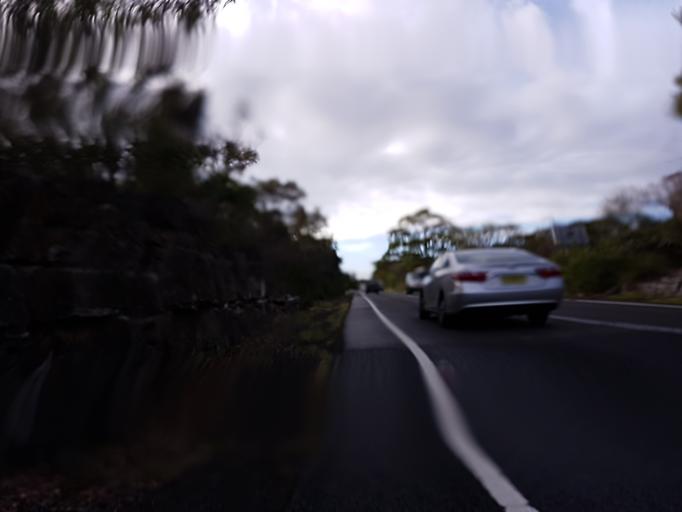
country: AU
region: New South Wales
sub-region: Warringah
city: Allambie Heights
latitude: -33.7736
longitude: 151.2368
